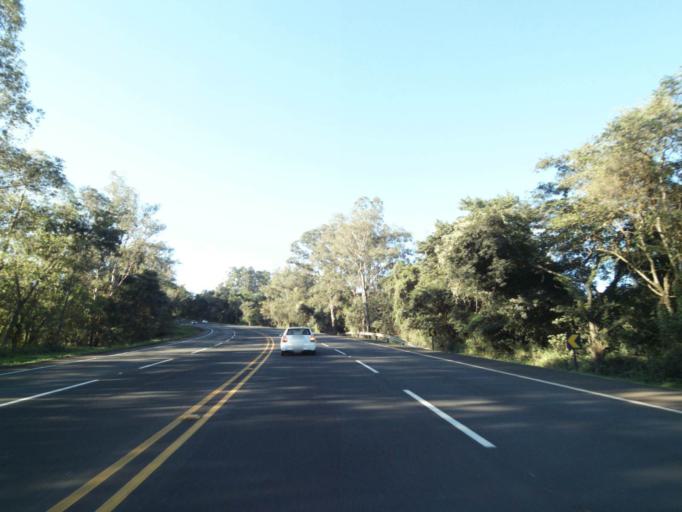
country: BR
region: Parana
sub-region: Arapongas
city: Arapongas
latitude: -23.4469
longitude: -51.5495
